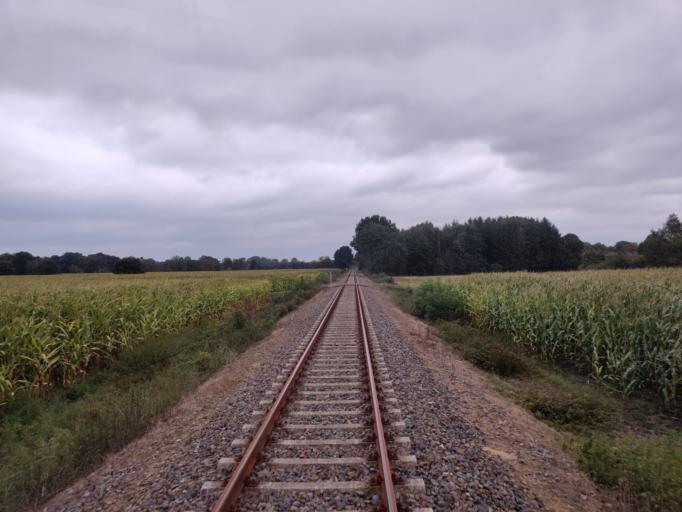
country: DE
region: Lower Saxony
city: Gnarrenburg
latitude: 53.3590
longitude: 9.0078
